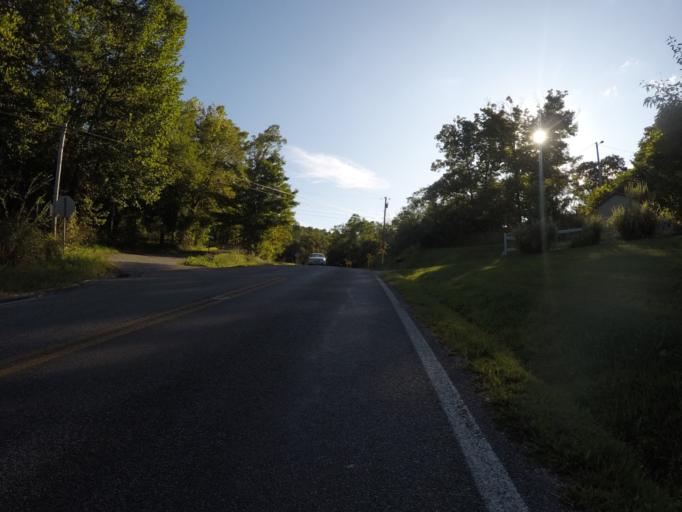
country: US
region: West Virginia
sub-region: Cabell County
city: Huntington
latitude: 38.4949
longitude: -82.4836
